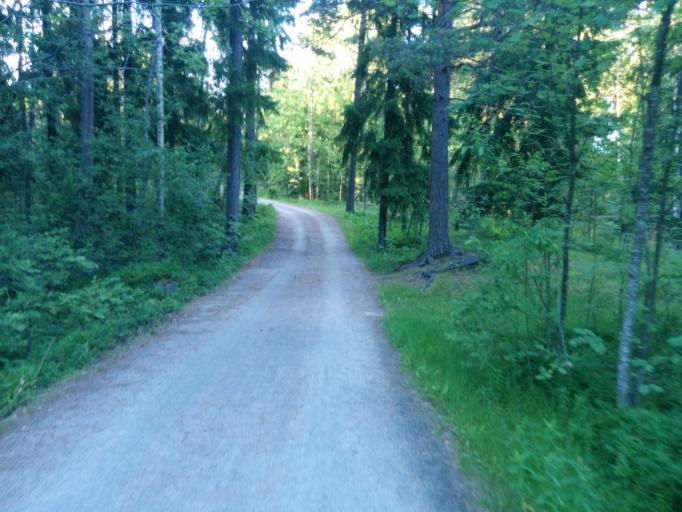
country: FI
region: Uusimaa
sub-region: Helsinki
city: Helsinki
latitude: 60.2148
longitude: 24.9161
